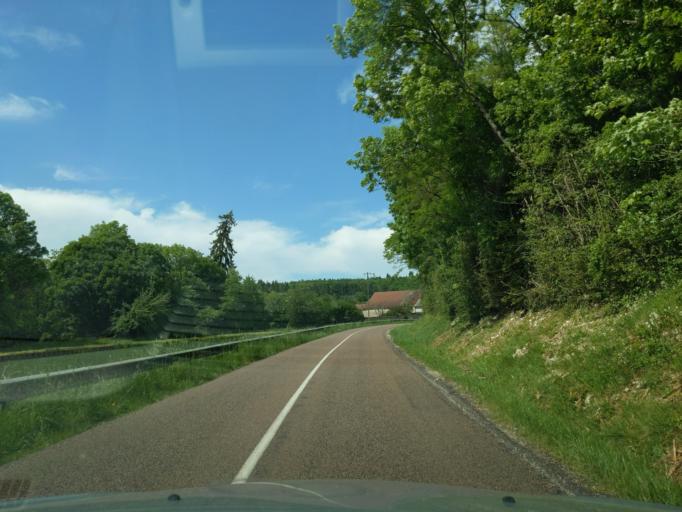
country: FR
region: Bourgogne
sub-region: Departement de la Cote-d'Or
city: Fleurey-sur-Ouche
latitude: 47.2945
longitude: 4.8144
